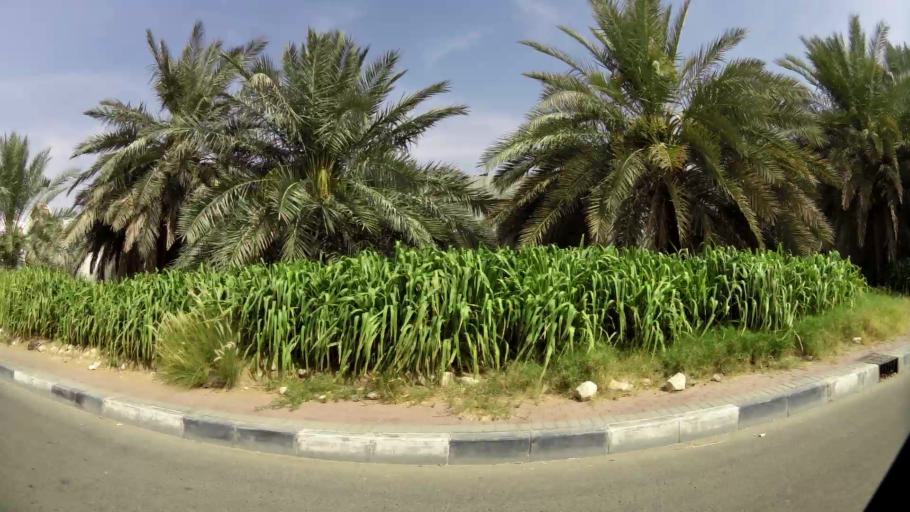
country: AE
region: Abu Dhabi
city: Al Ain
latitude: 24.1599
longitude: 55.6939
